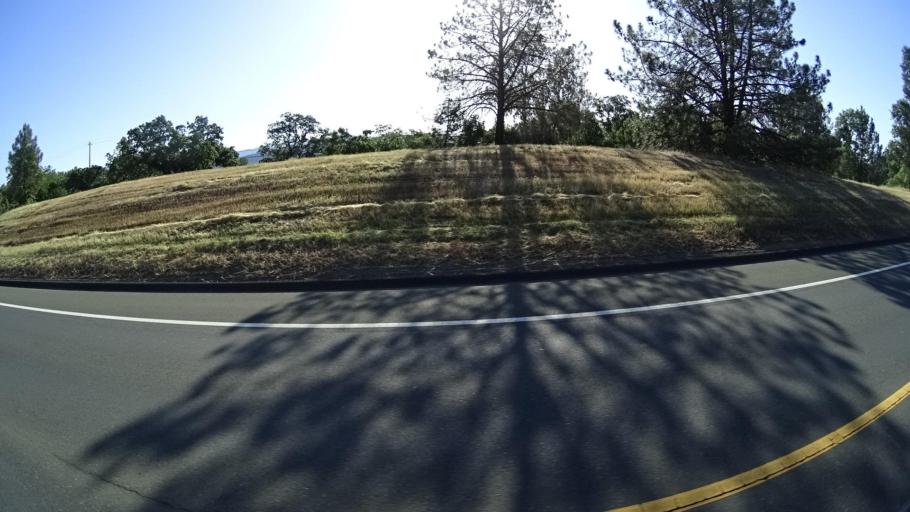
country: US
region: California
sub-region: Lake County
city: Upper Lake
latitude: 39.1330
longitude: -122.9088
